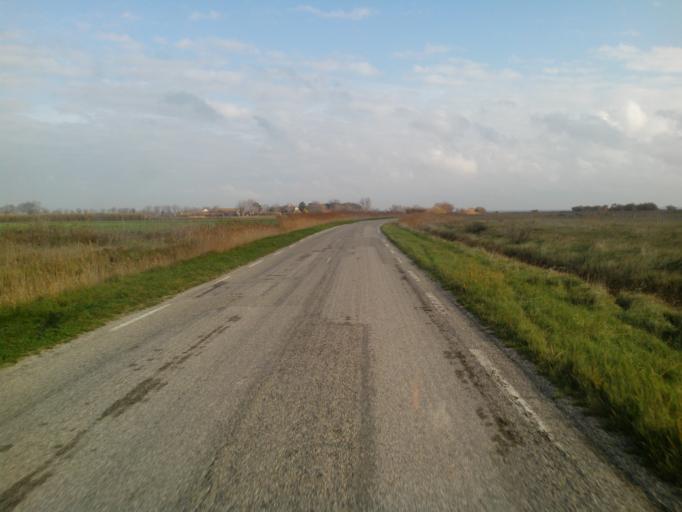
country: FR
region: Provence-Alpes-Cote d'Azur
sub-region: Departement des Bouches-du-Rhone
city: Arles
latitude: 43.5673
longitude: 4.5691
